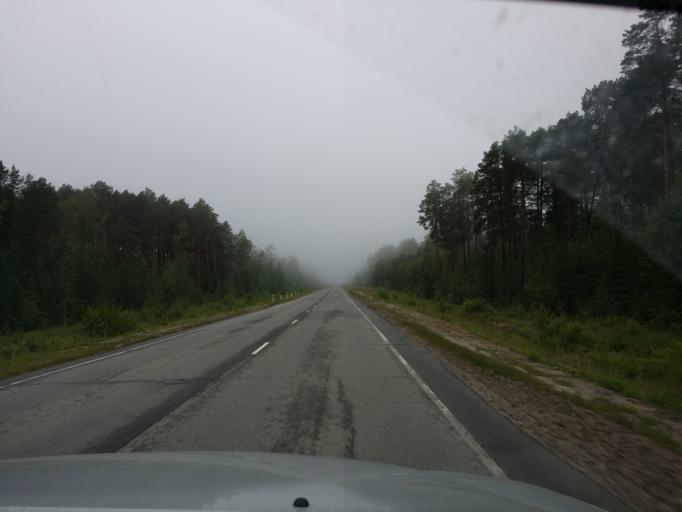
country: RU
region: Khanty-Mansiyskiy Avtonomnyy Okrug
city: Gornopravdinsk
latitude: 59.7129
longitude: 70.2245
